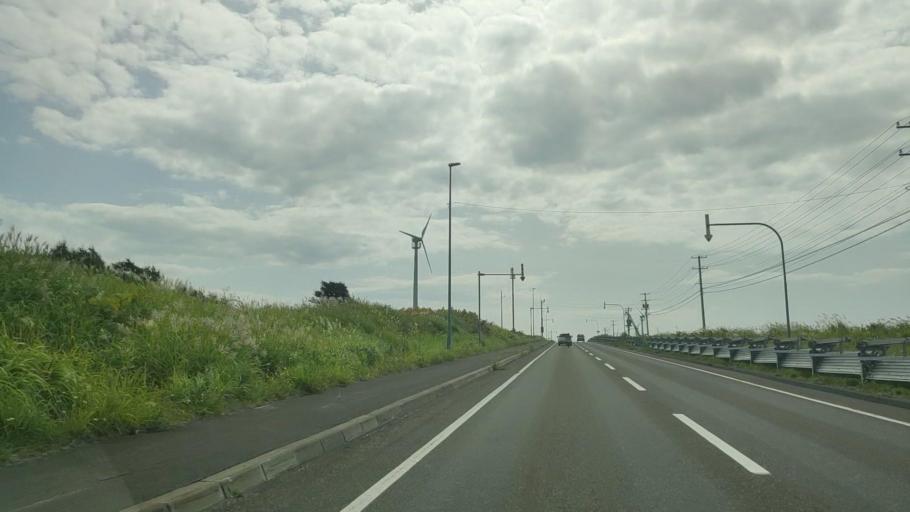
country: JP
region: Hokkaido
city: Rumoi
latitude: 44.4079
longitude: 141.7312
